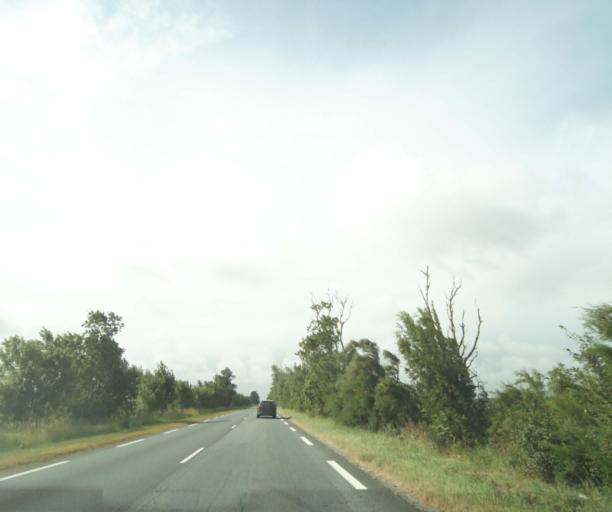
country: FR
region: Poitou-Charentes
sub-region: Departement de la Charente-Maritime
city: Andilly
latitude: 46.2613
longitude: -1.0670
